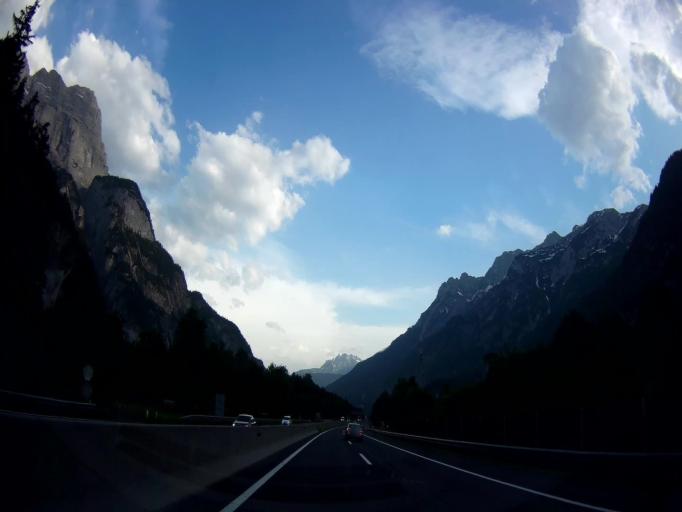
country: AT
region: Salzburg
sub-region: Politischer Bezirk Hallein
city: Golling an der Salzach
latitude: 47.5399
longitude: 13.1748
